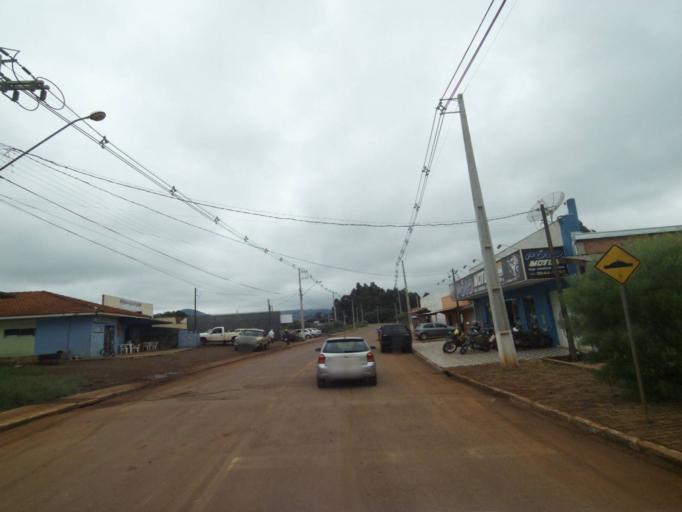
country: BR
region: Parana
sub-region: Pitanga
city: Pitanga
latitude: -24.9310
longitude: -51.8738
